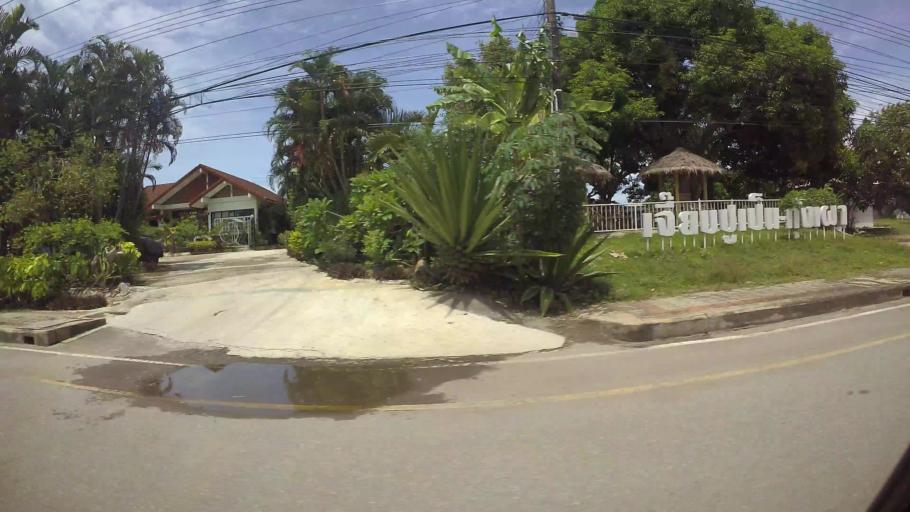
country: TH
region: Chon Buri
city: Sattahip
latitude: 12.7049
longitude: 100.8864
